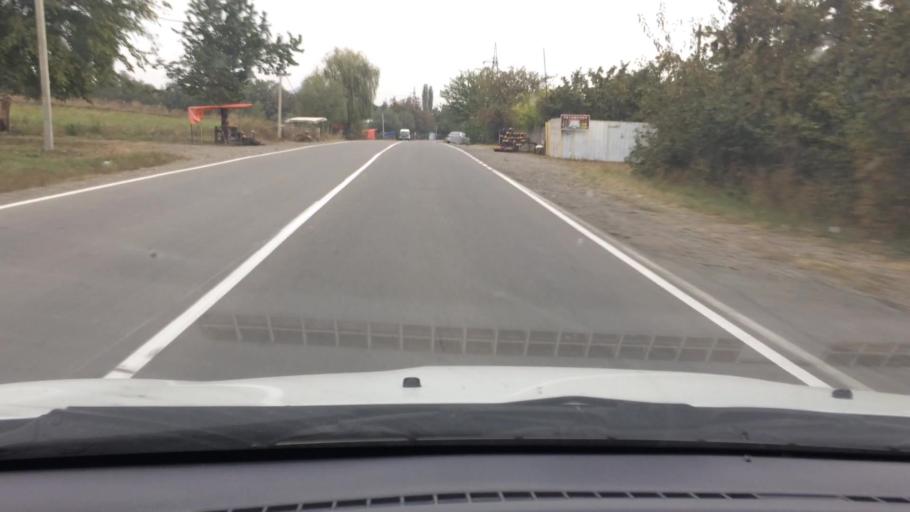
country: GE
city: Naghvarevi
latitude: 41.3210
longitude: 44.7967
